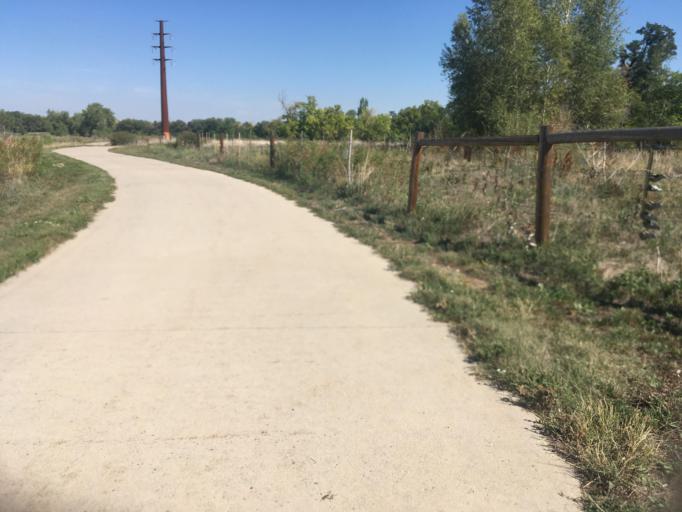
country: US
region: Colorado
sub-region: Boulder County
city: Boulder
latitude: 40.0220
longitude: -105.2337
